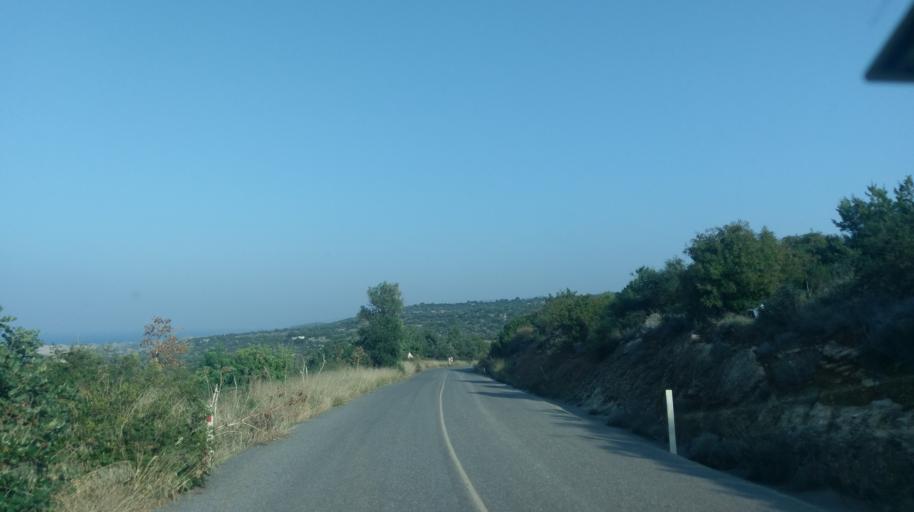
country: CY
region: Ammochostos
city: Leonarisso
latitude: 35.5498
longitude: 34.2262
